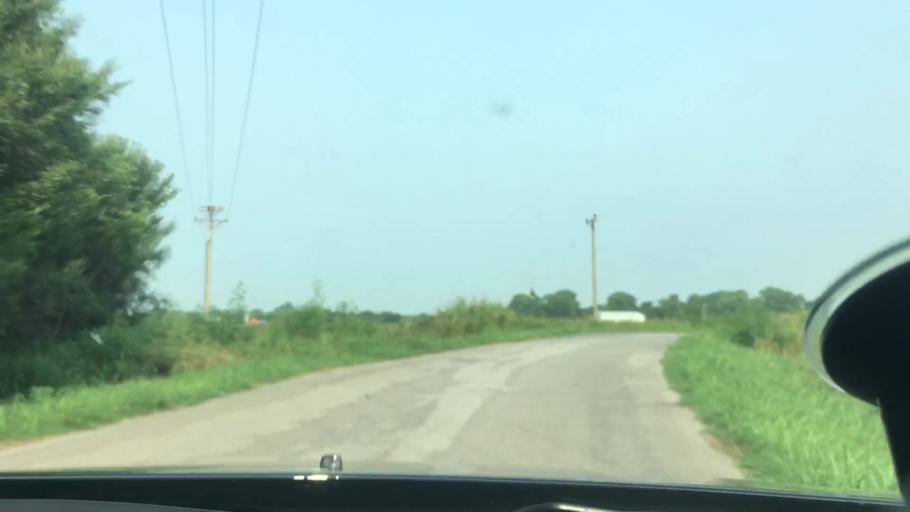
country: US
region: Oklahoma
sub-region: Garvin County
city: Lindsay
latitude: 34.8103
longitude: -97.6150
